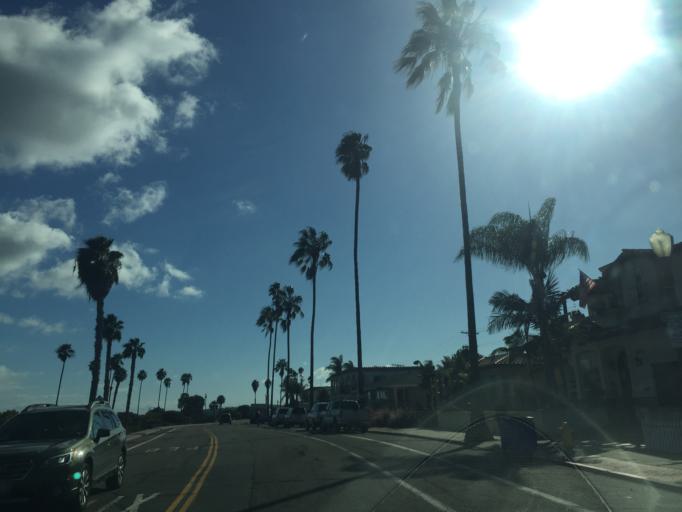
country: US
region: California
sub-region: San Diego County
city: La Jolla
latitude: 32.7871
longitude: -117.2346
